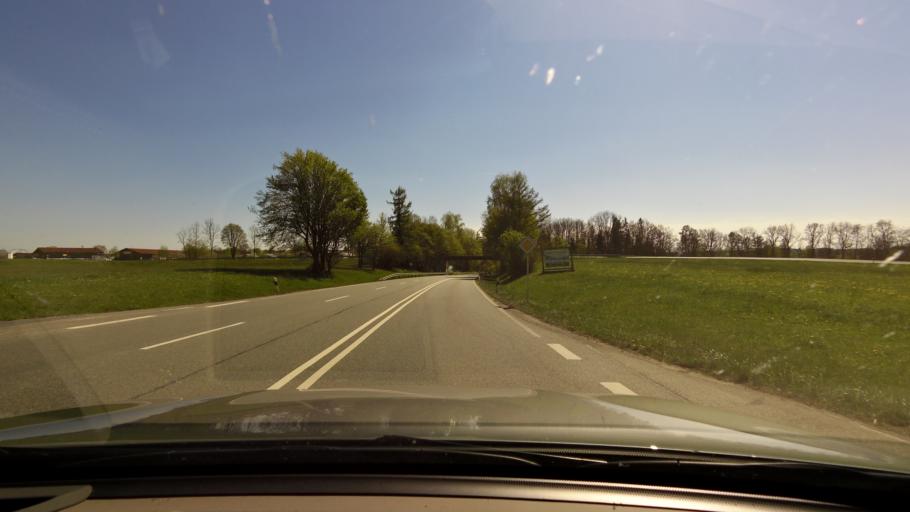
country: DE
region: Bavaria
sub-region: Upper Bavaria
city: Breitbrunn
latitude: 48.0312
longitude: 12.1774
